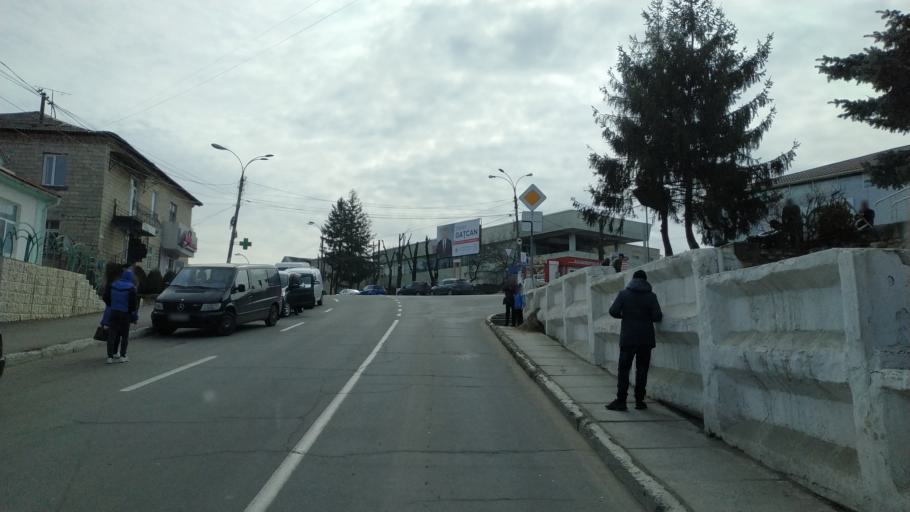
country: MD
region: Hincesti
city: Hincesti
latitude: 46.8285
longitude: 28.5889
